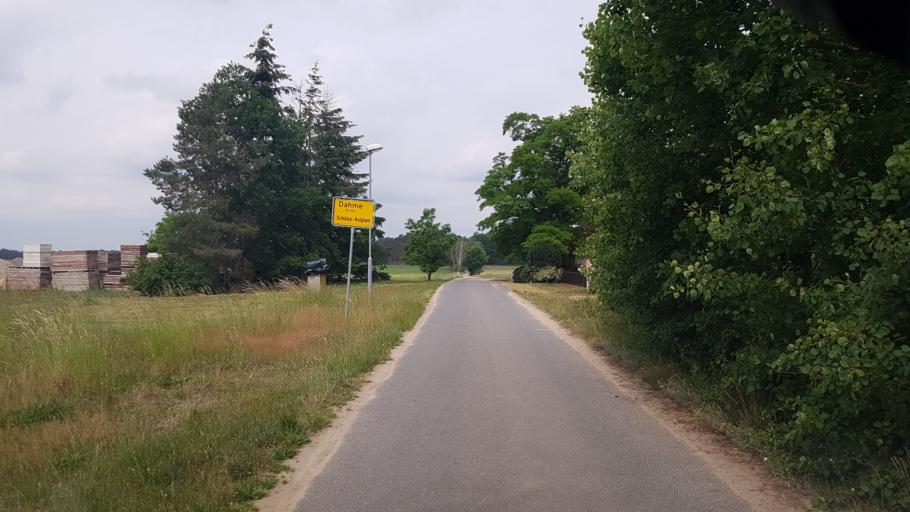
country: DE
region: Brandenburg
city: Lebusa
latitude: 51.8159
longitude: 13.4420
